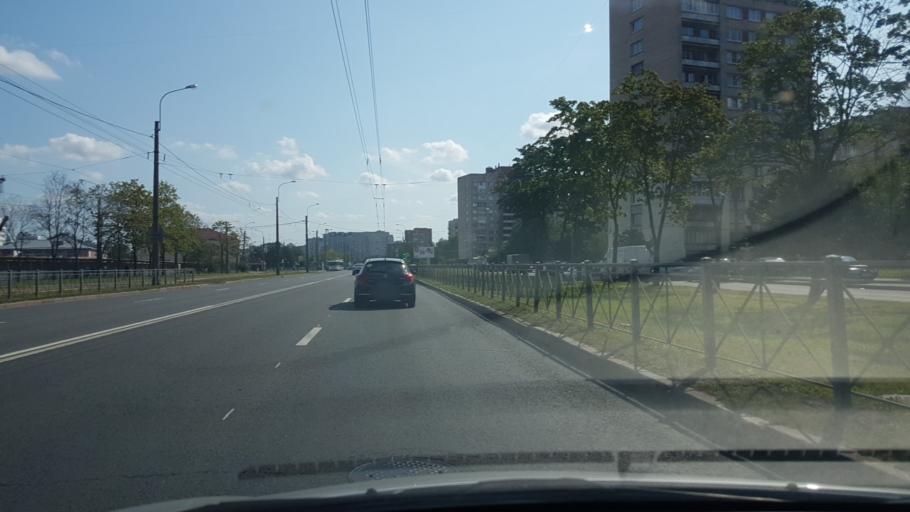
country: RU
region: St.-Petersburg
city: Sosnovaya Polyana
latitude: 59.8351
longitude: 30.1524
